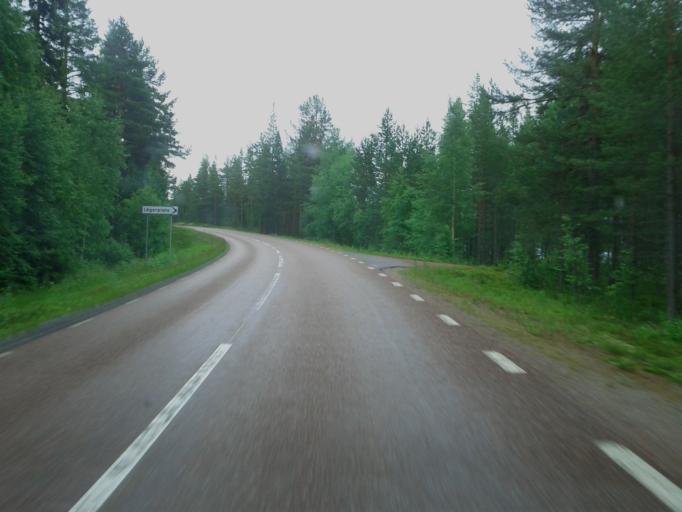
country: NO
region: Hedmark
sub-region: Trysil
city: Innbygda
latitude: 61.7867
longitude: 12.9308
